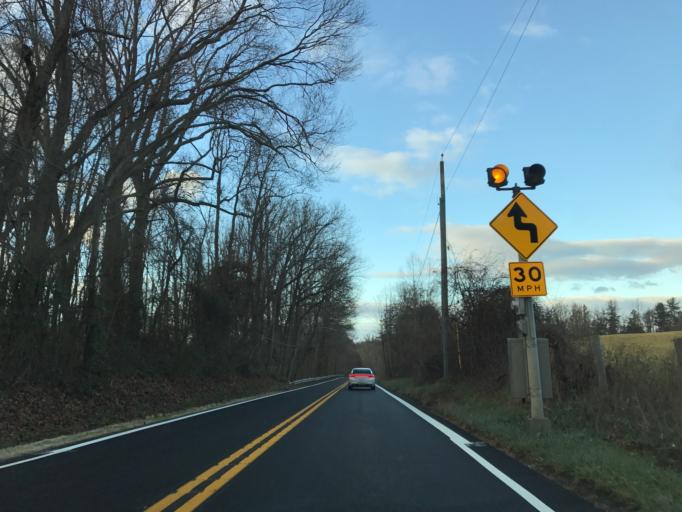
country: US
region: Maryland
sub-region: Harford County
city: Aberdeen
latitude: 39.6134
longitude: -76.1997
